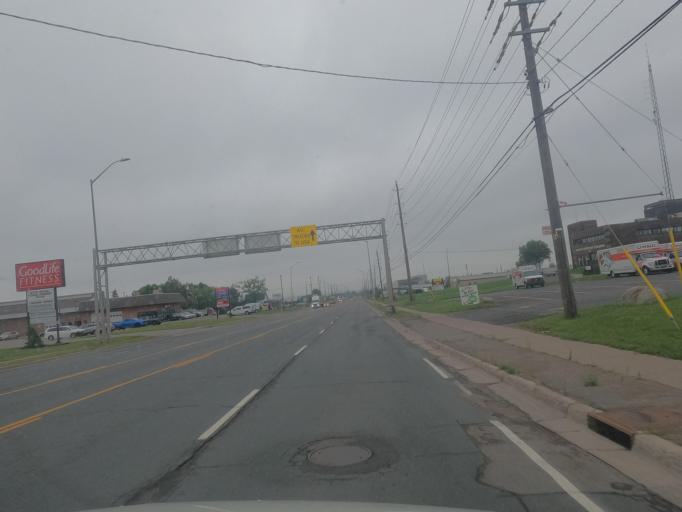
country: CA
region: Ontario
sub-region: Algoma
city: Sault Ste. Marie
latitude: 46.5385
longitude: -84.3210
